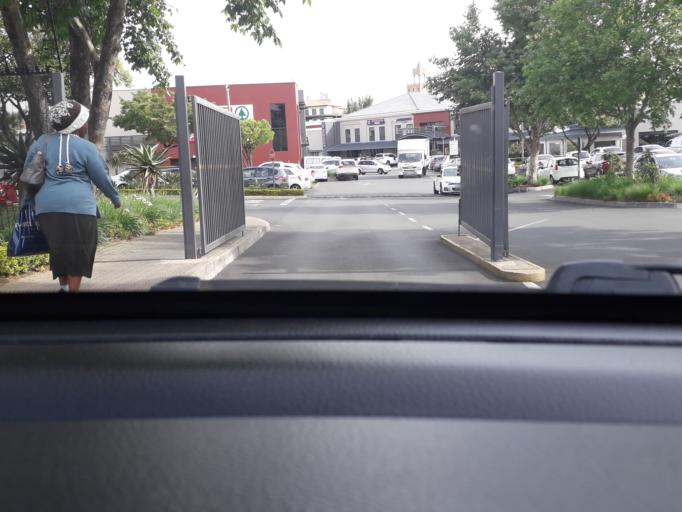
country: ZA
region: Gauteng
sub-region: City of Johannesburg Metropolitan Municipality
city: Diepsloot
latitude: -26.0210
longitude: 28.0151
